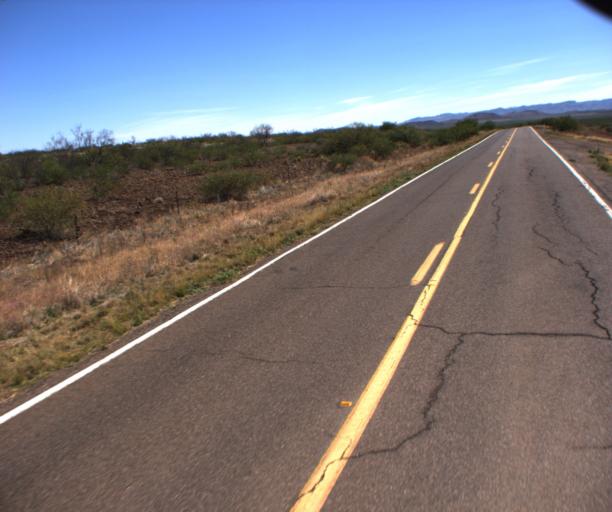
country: US
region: Arizona
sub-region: Cochise County
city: Douglas
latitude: 31.4603
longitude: -109.3700
